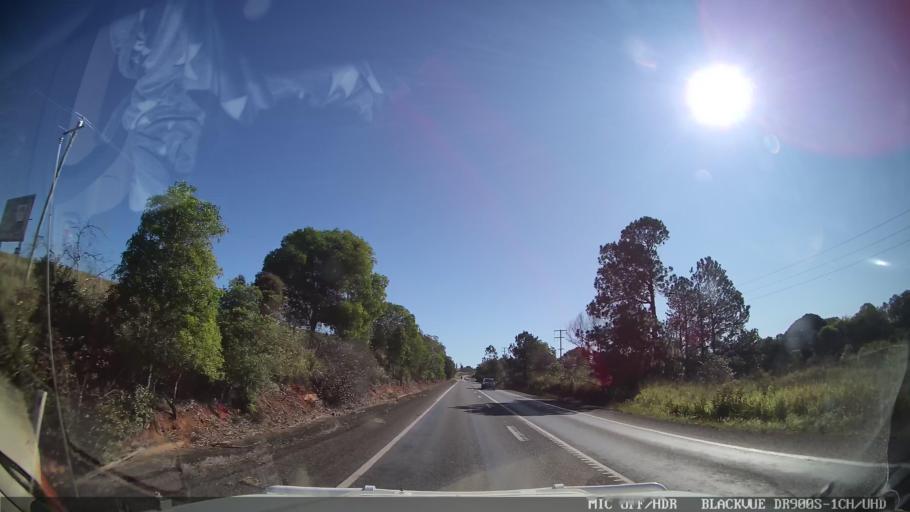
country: AU
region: Queensland
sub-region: Bundaberg
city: Childers
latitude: -25.2446
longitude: 152.3065
